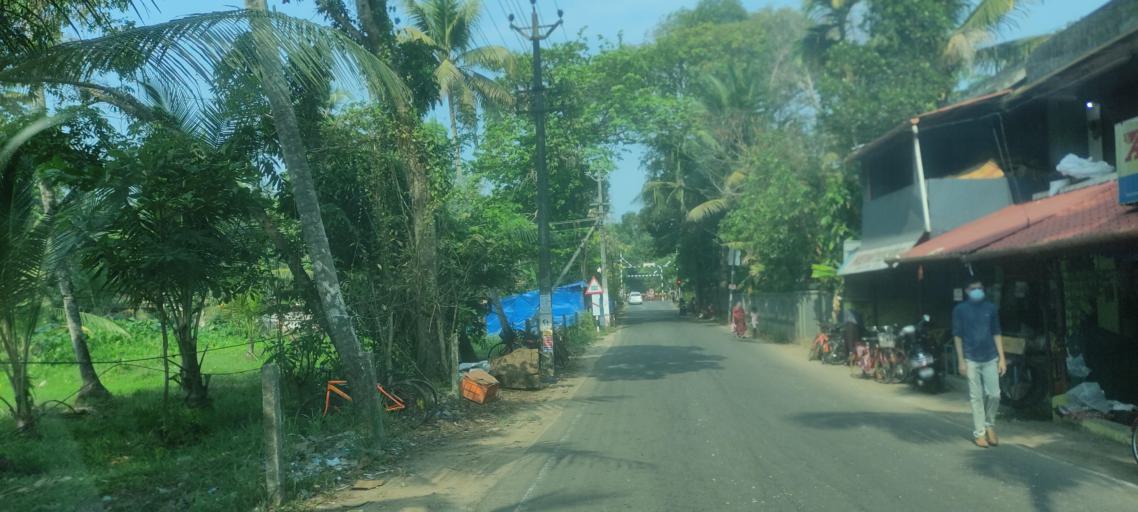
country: IN
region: Kerala
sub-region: Alappuzha
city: Kutiatodu
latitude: 9.7690
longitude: 76.3126
